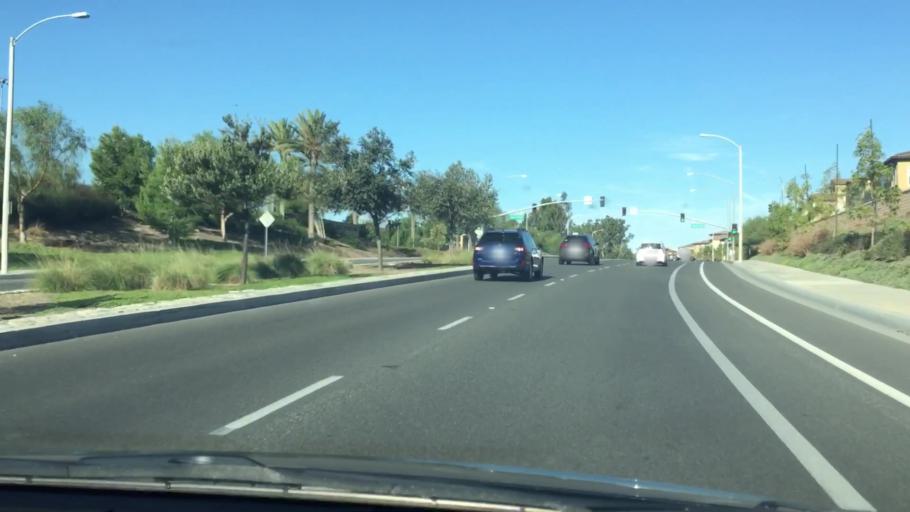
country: US
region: California
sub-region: Orange County
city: Foothill Ranch
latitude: 33.6656
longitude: -117.6537
